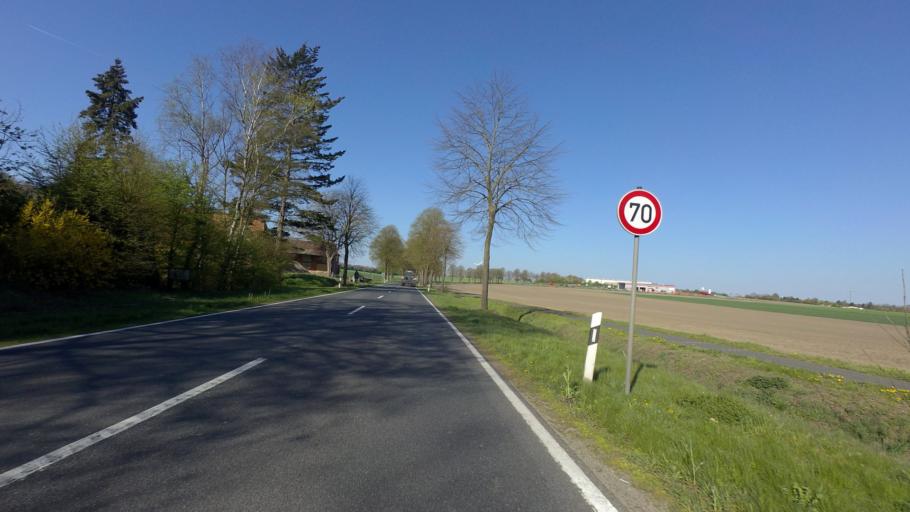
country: DE
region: Lower Saxony
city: Steimbke
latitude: 52.6520
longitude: 9.4150
